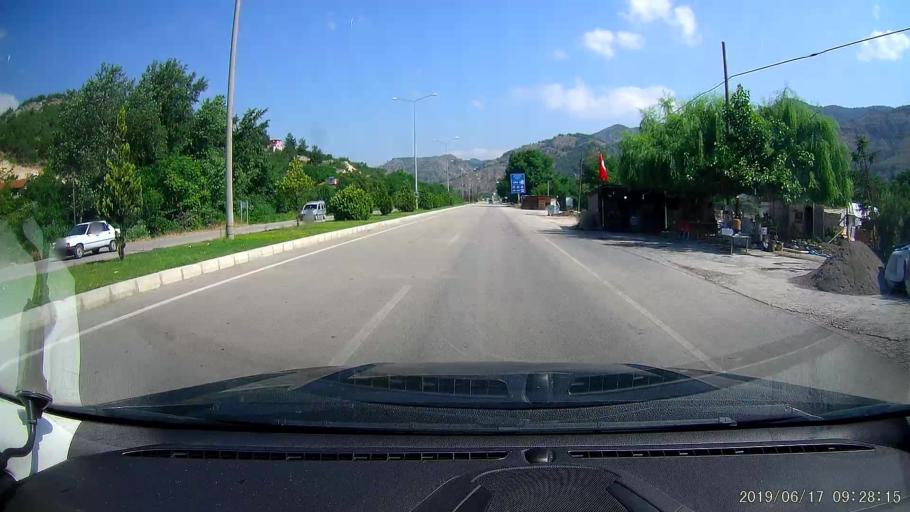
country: TR
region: Amasya
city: Amasya
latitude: 40.6862
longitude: 35.8228
